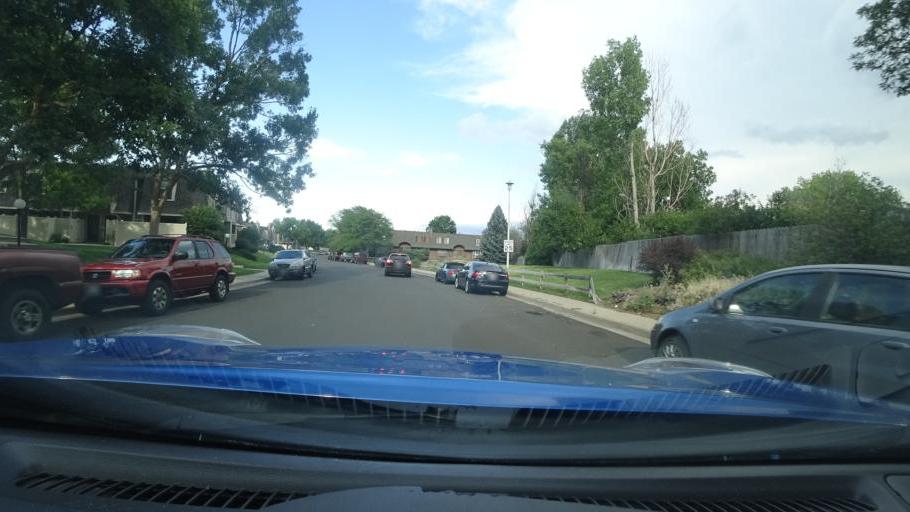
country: US
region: Colorado
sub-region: Adams County
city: Aurora
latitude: 39.6912
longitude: -104.8088
